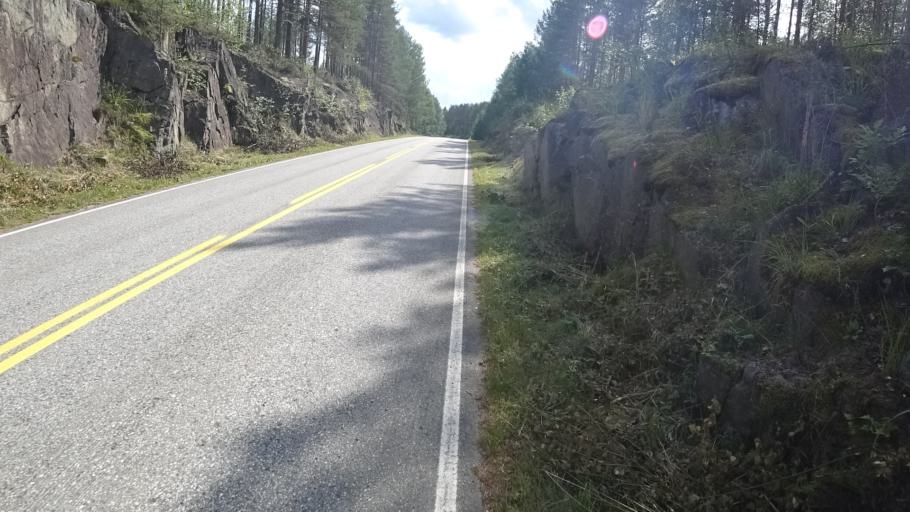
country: FI
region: North Karelia
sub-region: Joensuu
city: Ilomantsi
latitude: 62.6202
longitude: 31.2005
